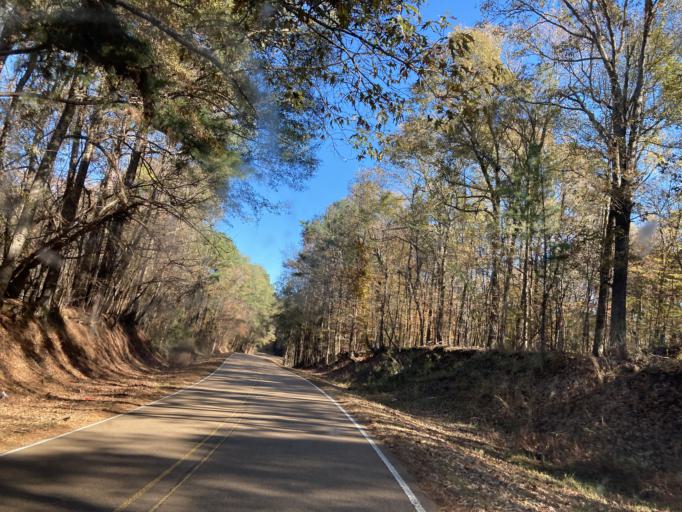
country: US
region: Mississippi
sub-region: Hinds County
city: Lynchburg
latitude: 32.5962
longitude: -90.5372
